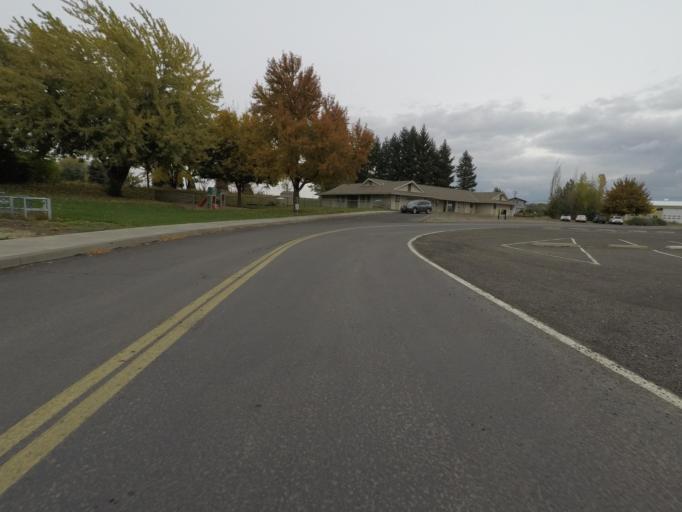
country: US
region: Washington
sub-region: Walla Walla County
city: Walla Walla East
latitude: 46.0801
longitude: -118.2748
